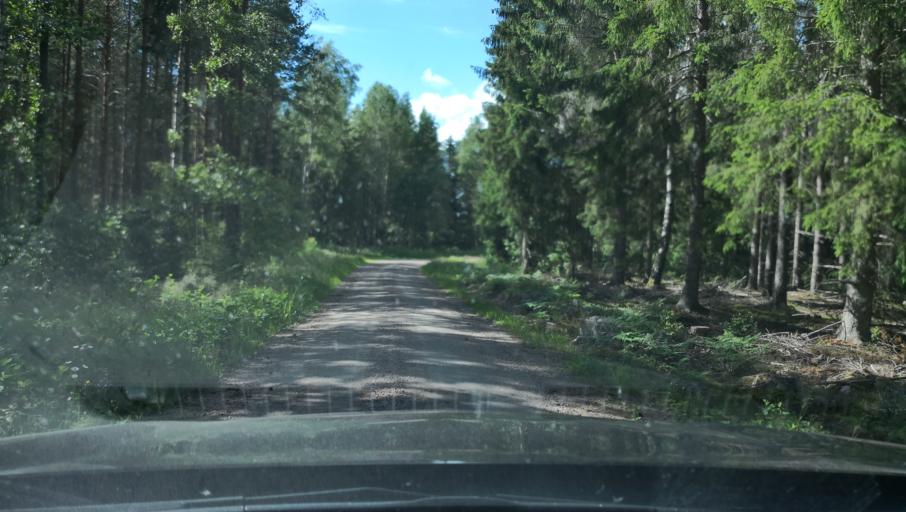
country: SE
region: Vaestmanland
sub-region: Arboga Kommun
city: Tyringe
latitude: 59.3284
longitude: 16.0301
